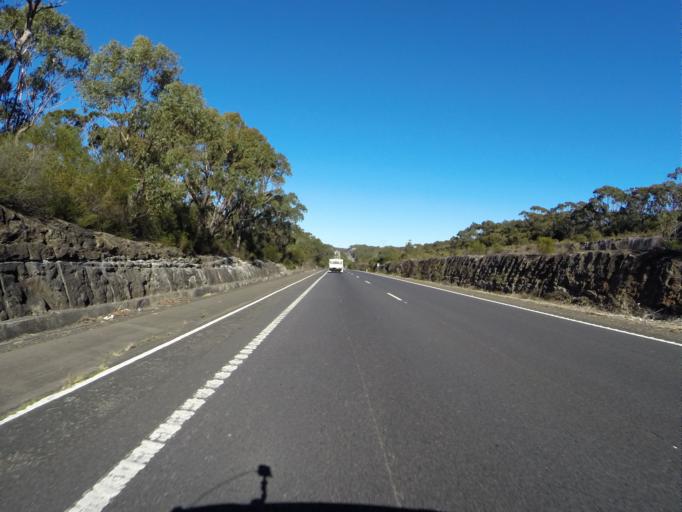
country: AU
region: New South Wales
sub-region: Wollongong
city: Helensburgh
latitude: -34.2128
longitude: 150.9593
